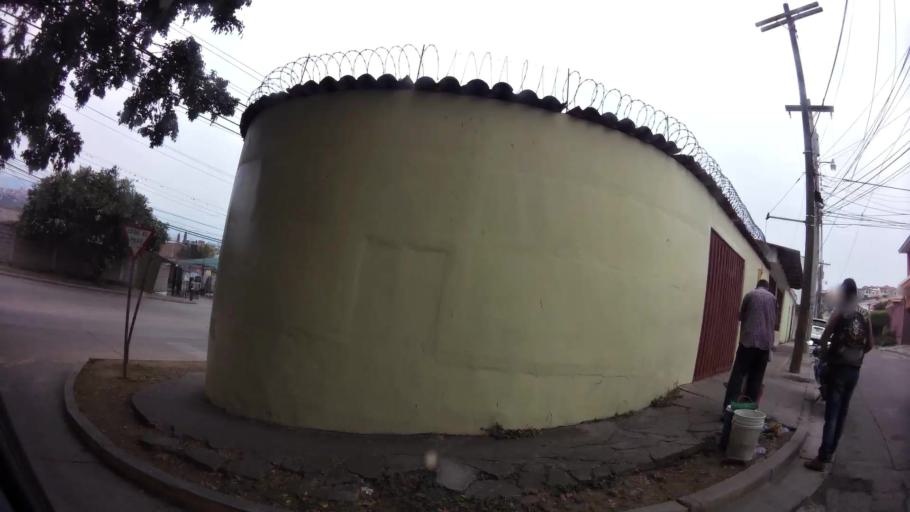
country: HN
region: Francisco Morazan
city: Tegucigalpa
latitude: 14.0728
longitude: -87.1953
